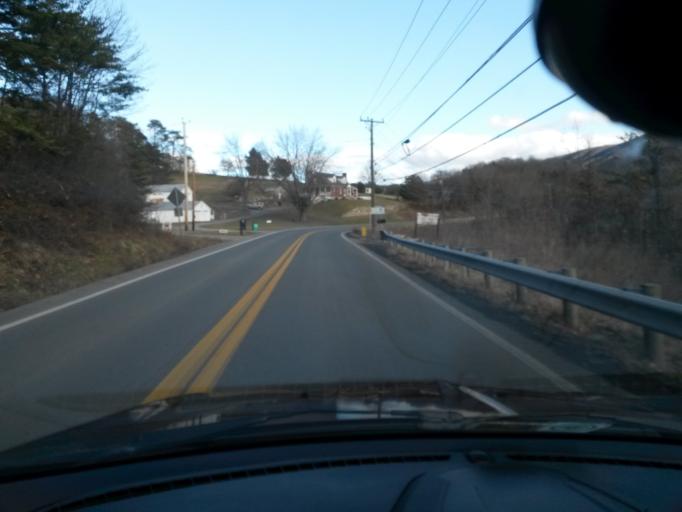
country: US
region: Virginia
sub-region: Giles County
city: Narrows
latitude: 37.3955
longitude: -80.7855
